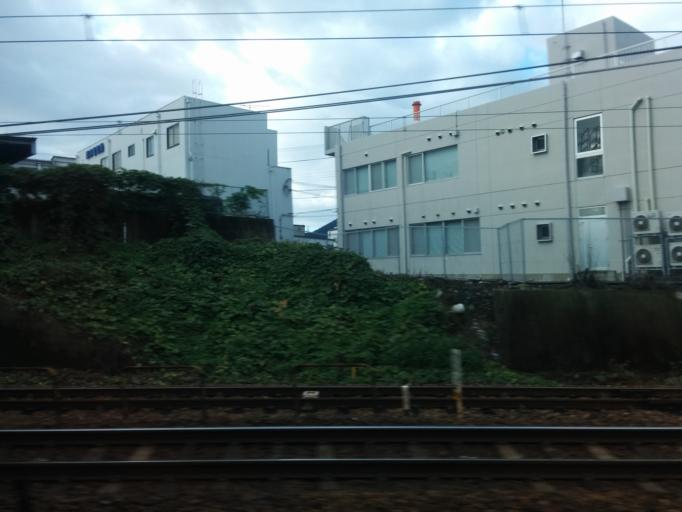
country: JP
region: Shiga Prefecture
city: Otsu-shi
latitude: 34.9811
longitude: 135.8960
